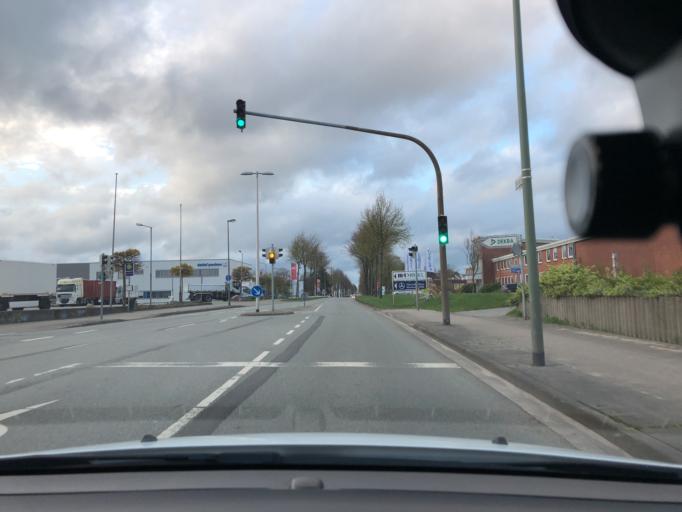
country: DE
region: Schleswig-Holstein
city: Flensburg
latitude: 54.7657
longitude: 9.4352
